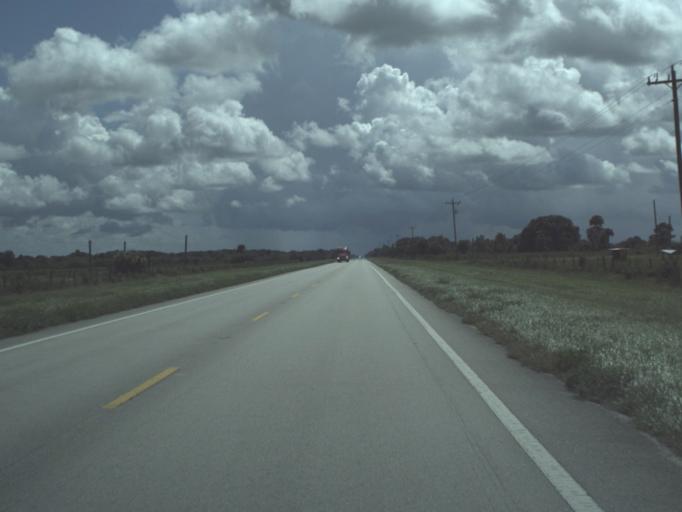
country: US
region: Florida
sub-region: Okeechobee County
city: Okeechobee
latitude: 27.3706
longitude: -80.9774
